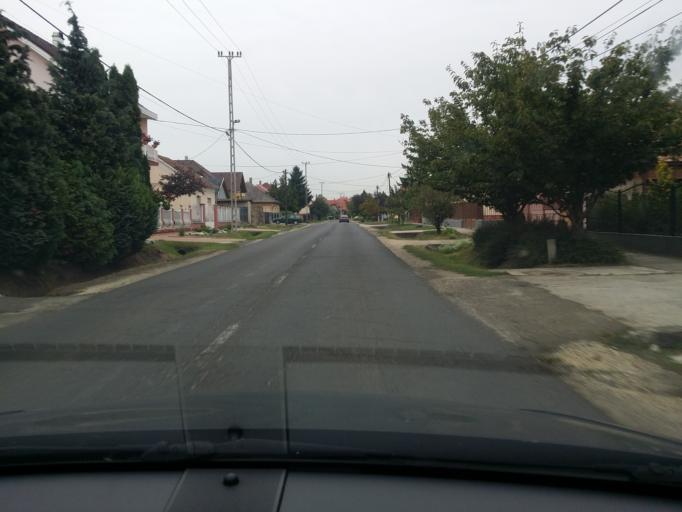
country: HU
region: Pest
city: Alsonemedi
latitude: 47.3199
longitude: 19.1527
